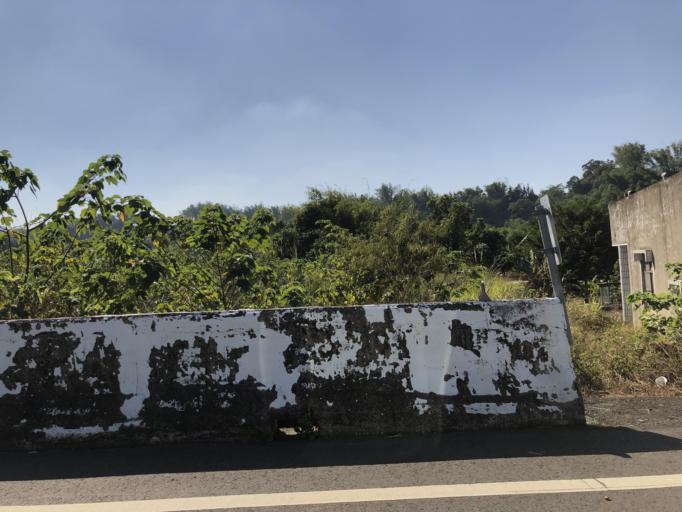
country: TW
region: Taiwan
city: Yujing
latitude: 23.0600
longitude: 120.3929
